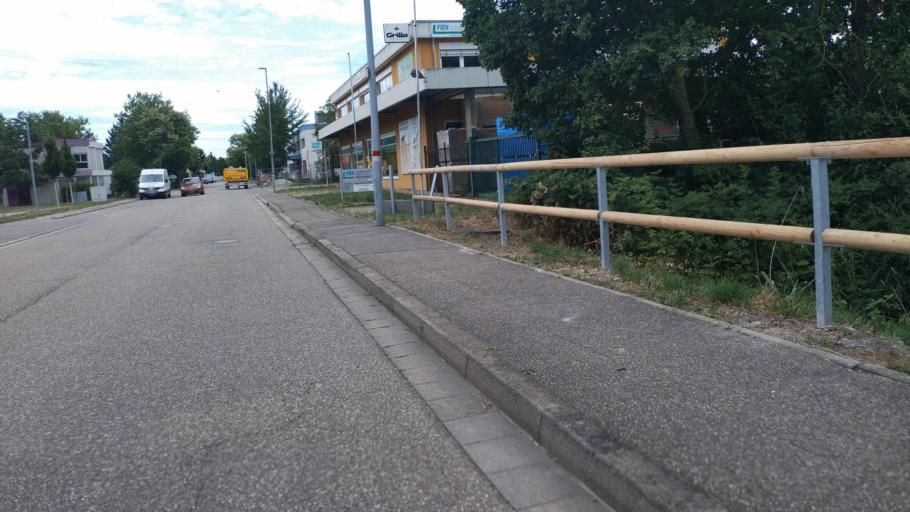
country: DE
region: Baden-Wuerttemberg
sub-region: Karlsruhe Region
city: Ettlingen
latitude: 48.9372
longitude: 8.3769
